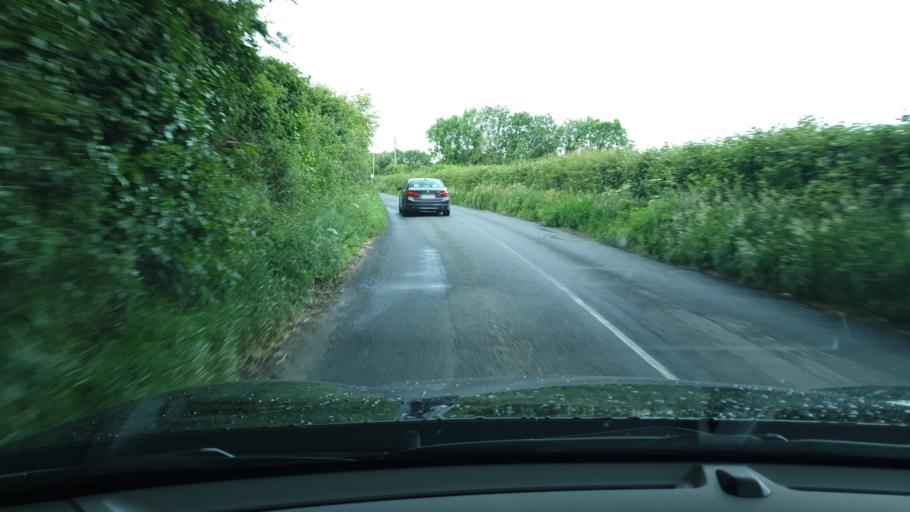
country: IE
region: Leinster
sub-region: An Mhi
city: Ashbourne
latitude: 53.5667
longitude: -6.3653
